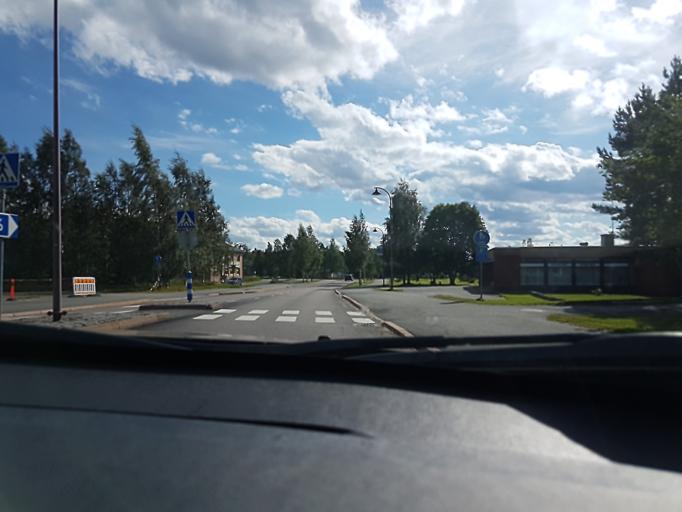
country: FI
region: Southern Ostrobothnia
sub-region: Jaerviseutu
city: Soini
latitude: 62.8733
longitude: 24.2063
